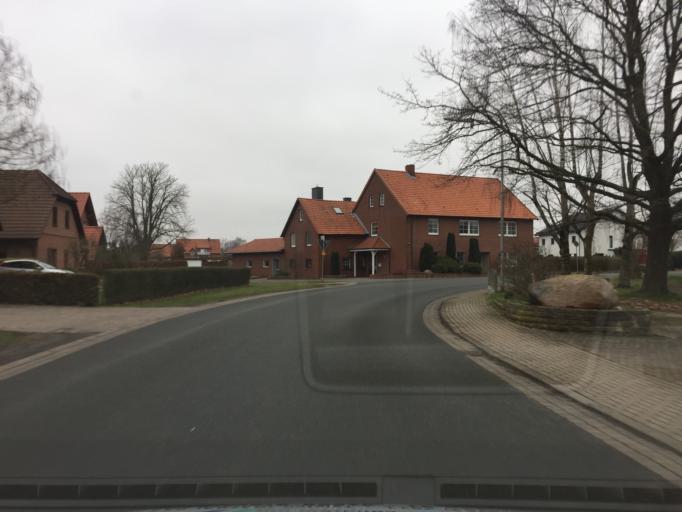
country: DE
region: Lower Saxony
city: Niedernwohren
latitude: 52.3518
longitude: 9.1397
